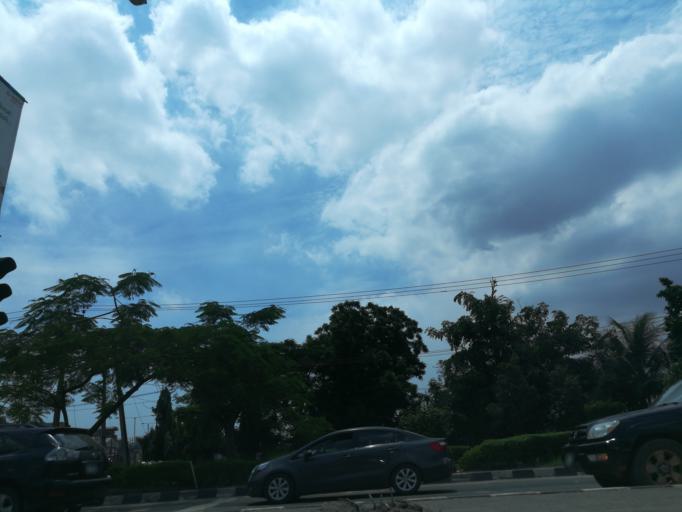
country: NG
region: Lagos
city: Ikeja
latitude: 6.6097
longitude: 3.3525
